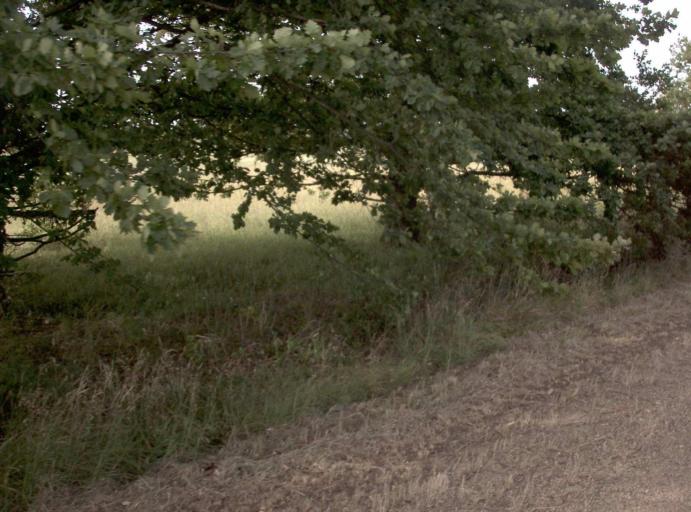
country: AU
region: Victoria
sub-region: Wellington
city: Heyfield
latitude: -38.0147
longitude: 146.7733
